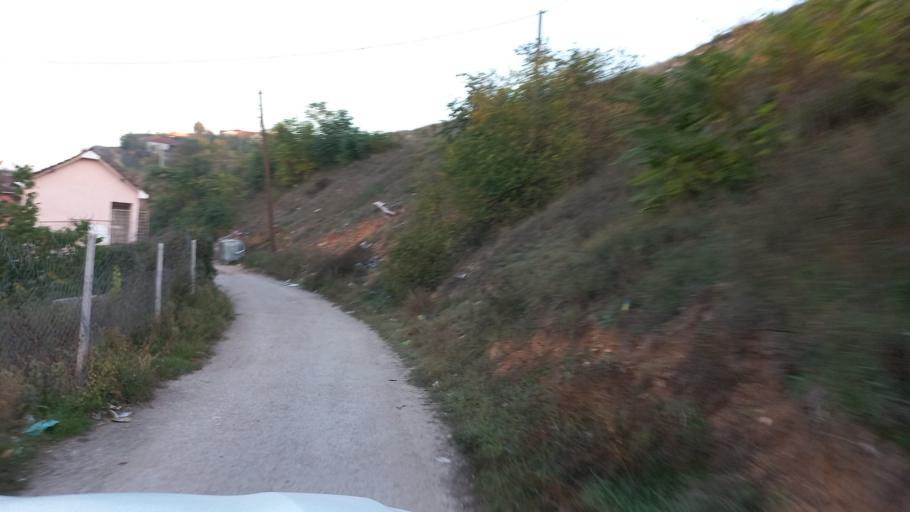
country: MK
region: Kumanovo
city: Kumanovo
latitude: 42.1387
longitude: 21.7279
